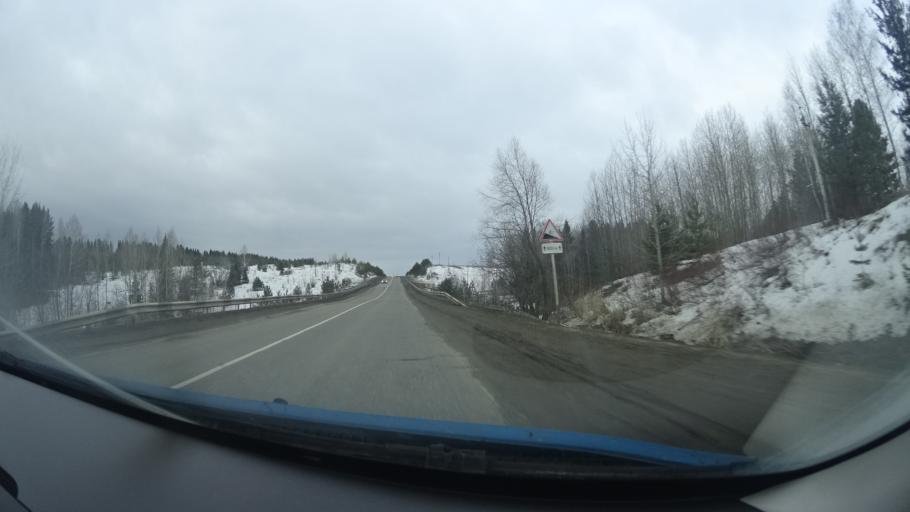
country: RU
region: Perm
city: Osa
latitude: 57.2373
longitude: 55.5958
